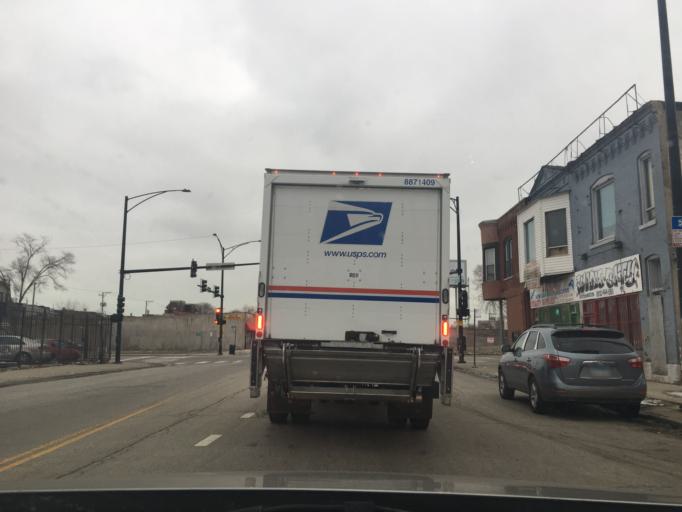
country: US
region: Illinois
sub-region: Cook County
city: Chicago
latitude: 41.8810
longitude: -87.7018
